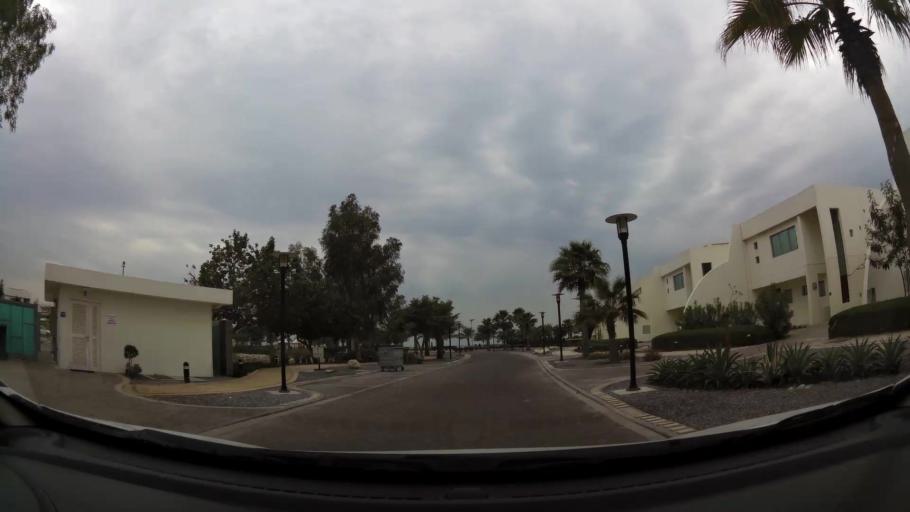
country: BH
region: Central Governorate
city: Dar Kulayb
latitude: 25.8430
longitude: 50.6103
